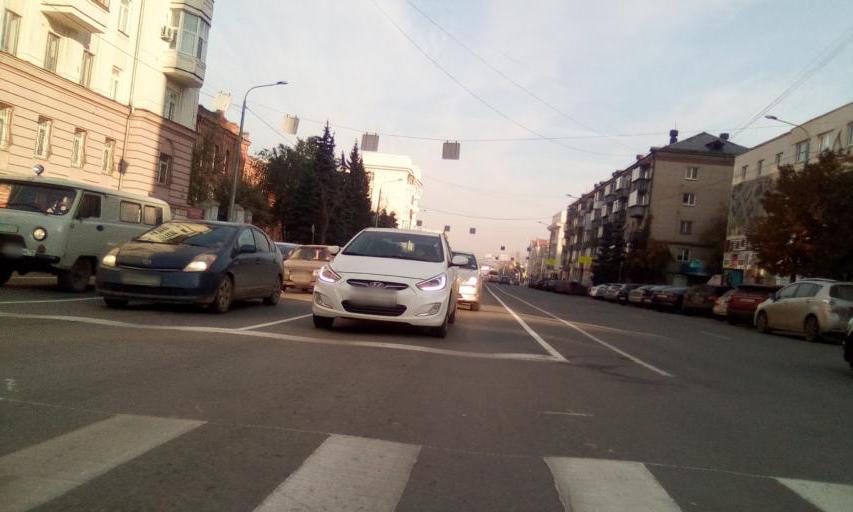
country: RU
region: Chelyabinsk
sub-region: Gorod Chelyabinsk
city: Chelyabinsk
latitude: 55.1581
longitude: 61.3946
